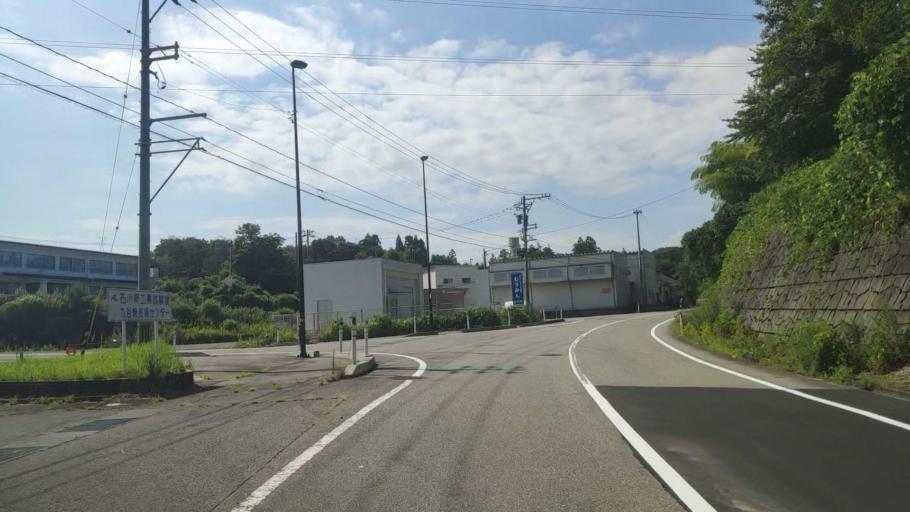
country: JP
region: Ishikawa
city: Komatsu
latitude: 36.3879
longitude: 136.4957
